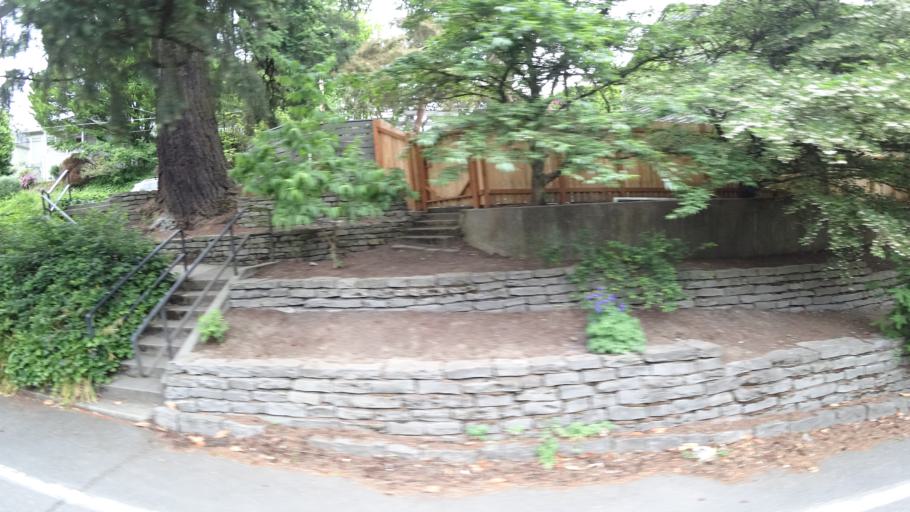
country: US
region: Oregon
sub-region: Multnomah County
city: Portland
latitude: 45.5055
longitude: -122.7025
